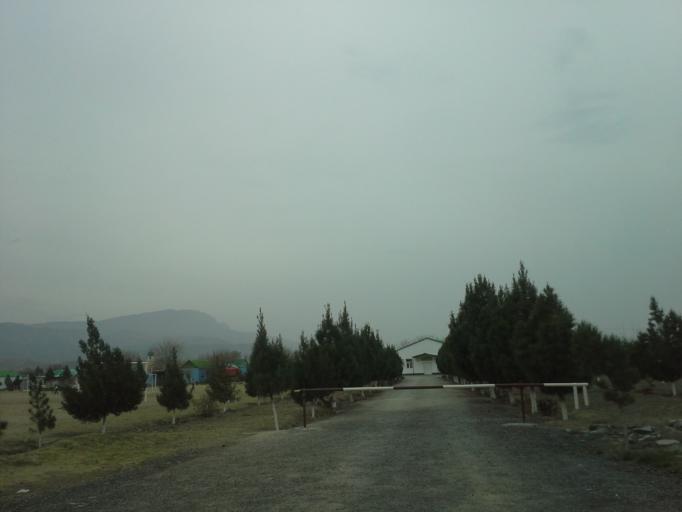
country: TM
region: Ahal
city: Abadan
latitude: 37.9802
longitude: 58.2181
